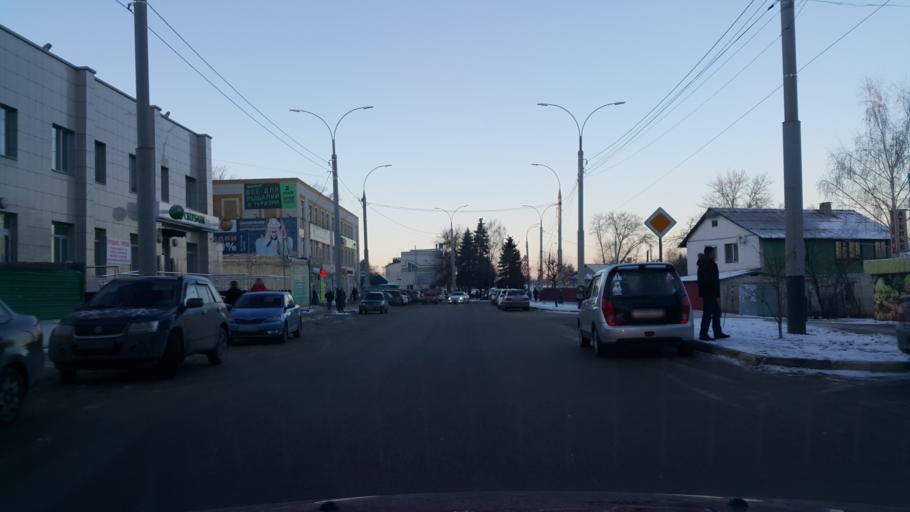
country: RU
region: Tambov
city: Pokrovo-Prigorodnoye
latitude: 52.7087
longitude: 41.3972
